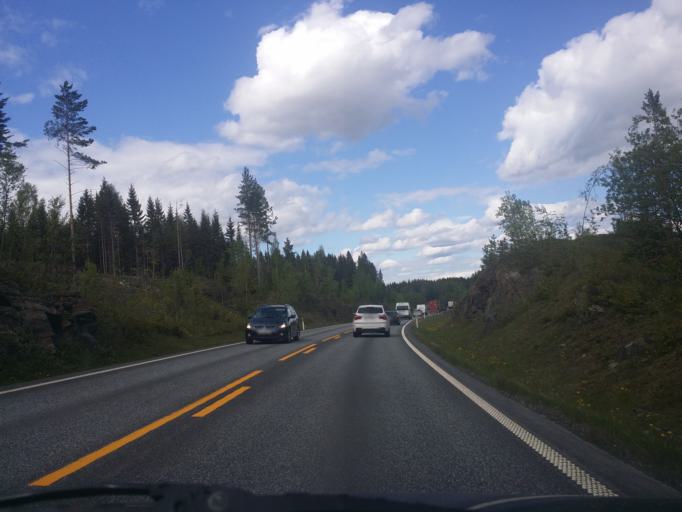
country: NO
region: Oppland
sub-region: Lunner
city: Roa
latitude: 60.2731
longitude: 10.5062
